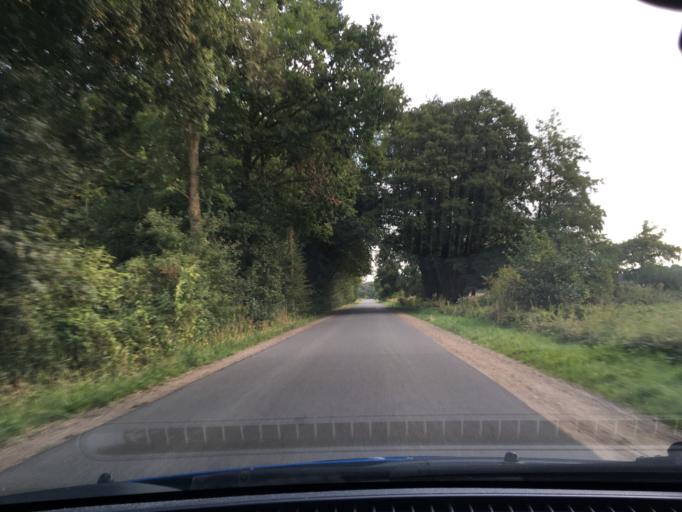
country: DE
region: Lower Saxony
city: Garstedt
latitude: 53.2827
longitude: 10.1719
